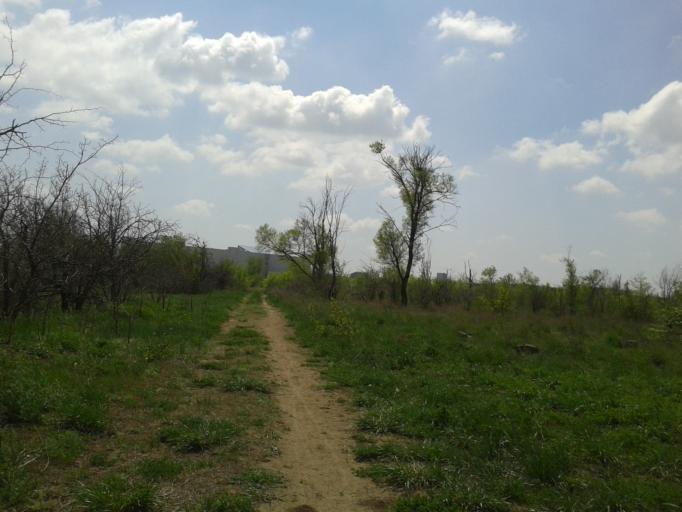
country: RU
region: Volgograd
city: Volgograd
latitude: 48.6426
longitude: 44.4373
